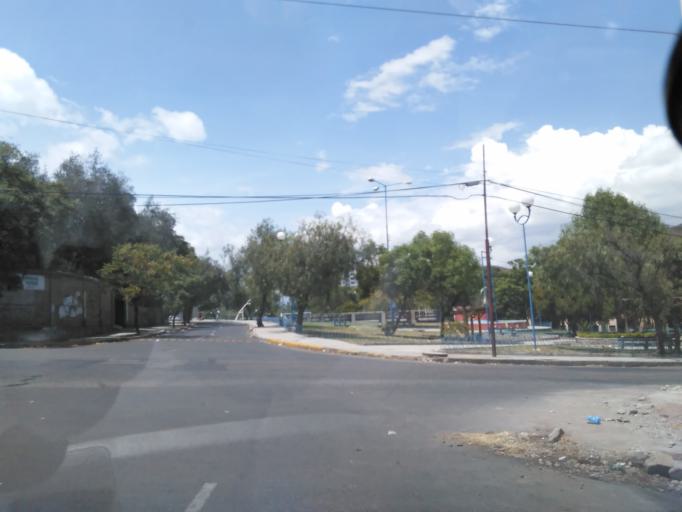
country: BO
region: Cochabamba
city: Cochabamba
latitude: -17.3723
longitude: -66.1415
